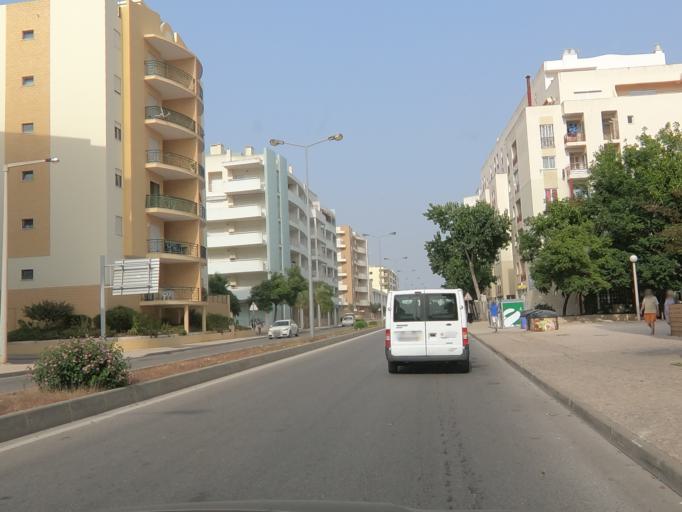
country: PT
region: Faro
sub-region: Silves
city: Armacao de Pera
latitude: 37.1042
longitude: -8.3625
